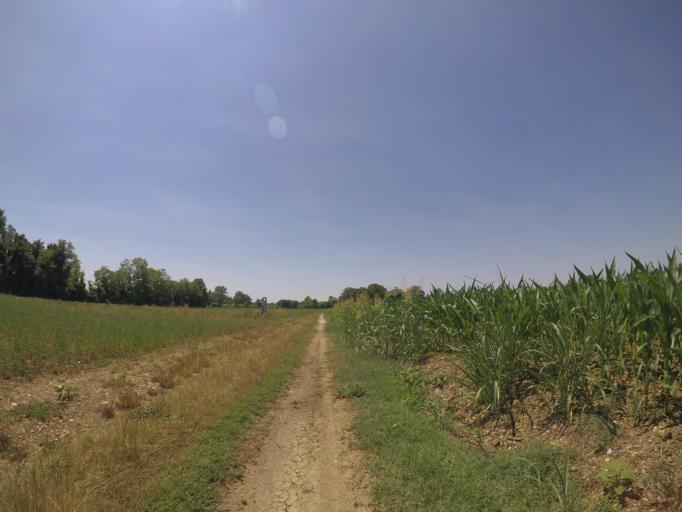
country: IT
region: Friuli Venezia Giulia
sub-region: Provincia di Udine
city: Talmassons
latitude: 45.9247
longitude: 13.0945
